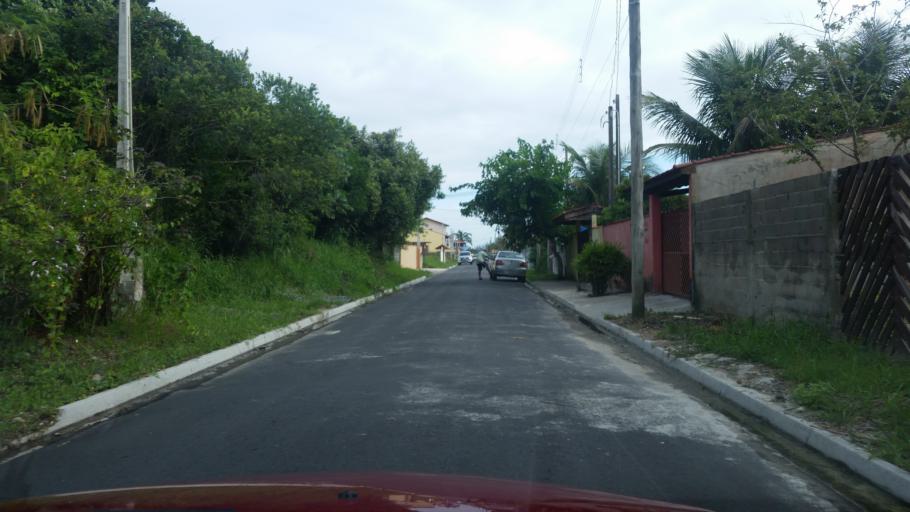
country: BR
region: Sao Paulo
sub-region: Iguape
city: Iguape
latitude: -24.7383
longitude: -47.5518
